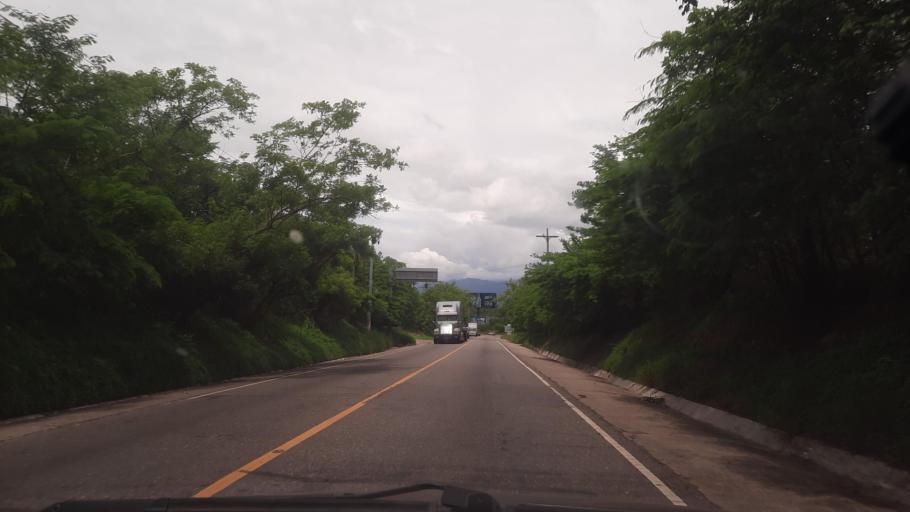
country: GT
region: Zacapa
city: Rio Hondo
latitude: 15.0369
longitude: -89.5895
